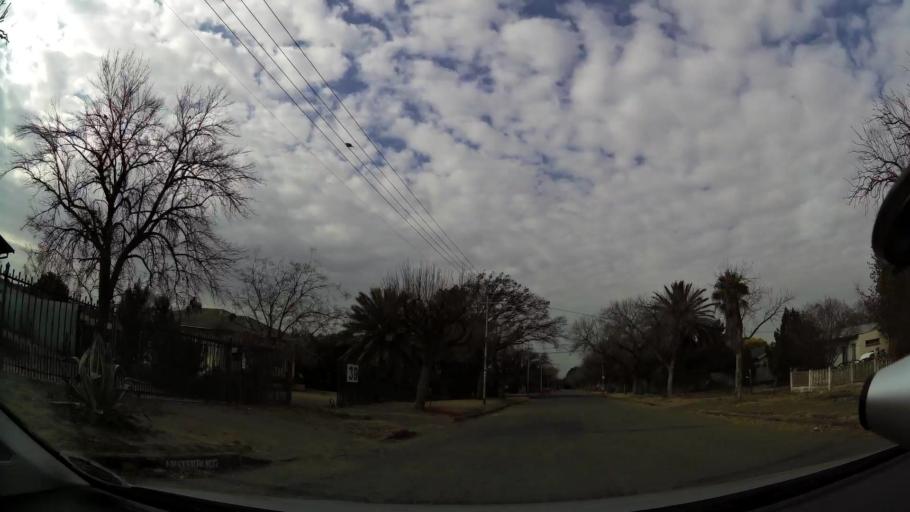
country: ZA
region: Orange Free State
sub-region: Mangaung Metropolitan Municipality
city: Bloemfontein
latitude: -29.0858
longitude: 26.2510
